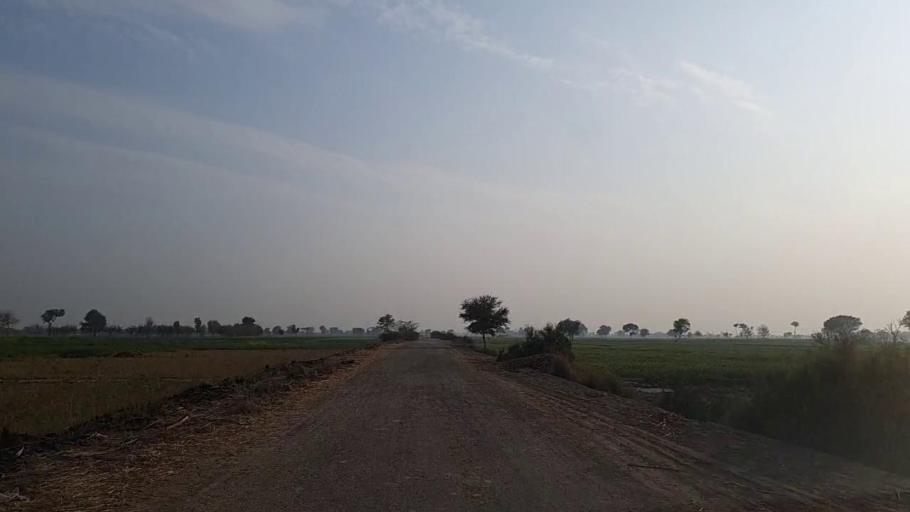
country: PK
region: Sindh
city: Jam Sahib
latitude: 26.3205
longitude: 68.5337
